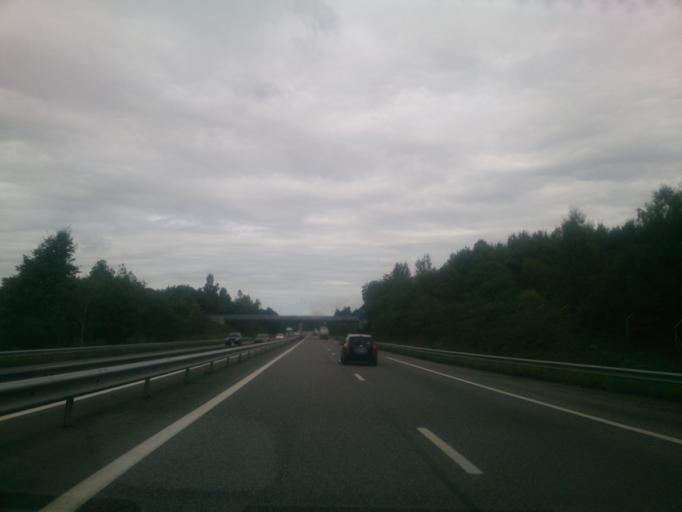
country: FR
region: Midi-Pyrenees
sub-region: Departement de la Haute-Garonne
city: Montrejeau
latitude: 43.1014
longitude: 0.4838
